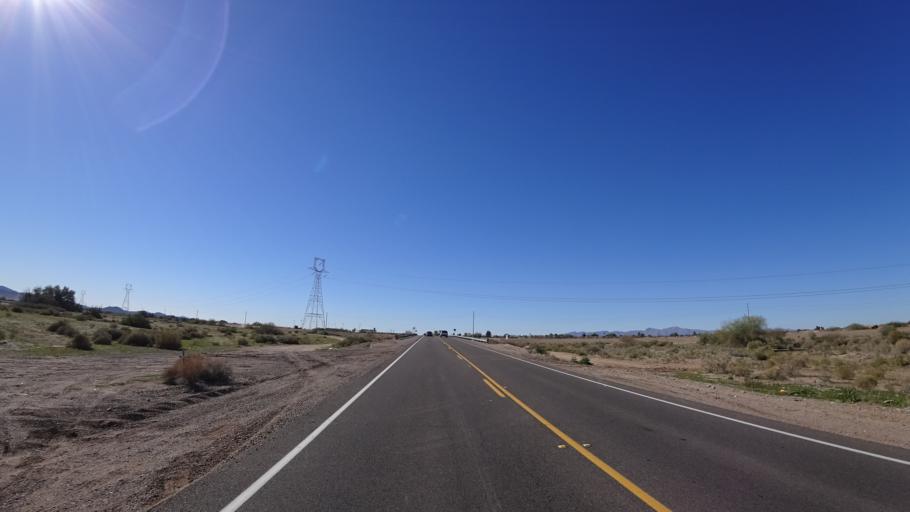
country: US
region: Arizona
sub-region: Maricopa County
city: Avondale
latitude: 33.4208
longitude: -112.3392
